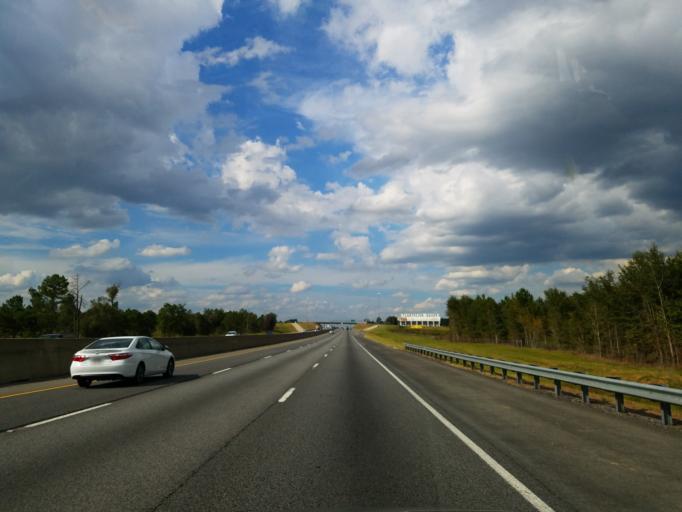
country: US
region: Georgia
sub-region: Turner County
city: Ashburn
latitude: 31.8295
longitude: -83.7122
